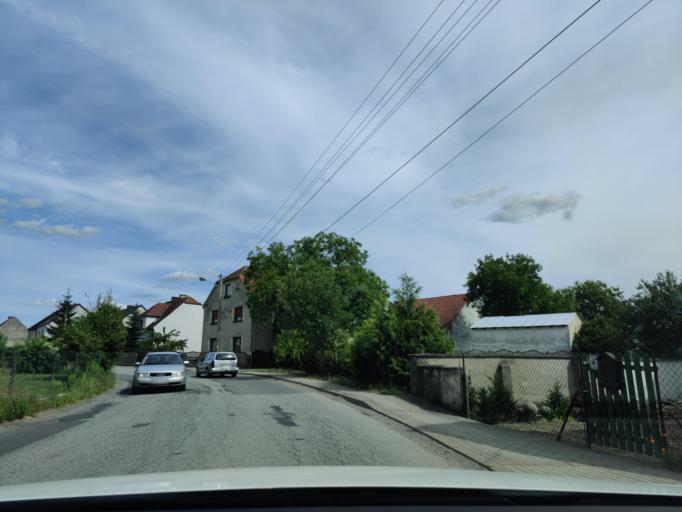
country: PL
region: Opole Voivodeship
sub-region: Powiat krapkowicki
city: Strzeleczki
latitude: 50.4552
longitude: 17.8465
